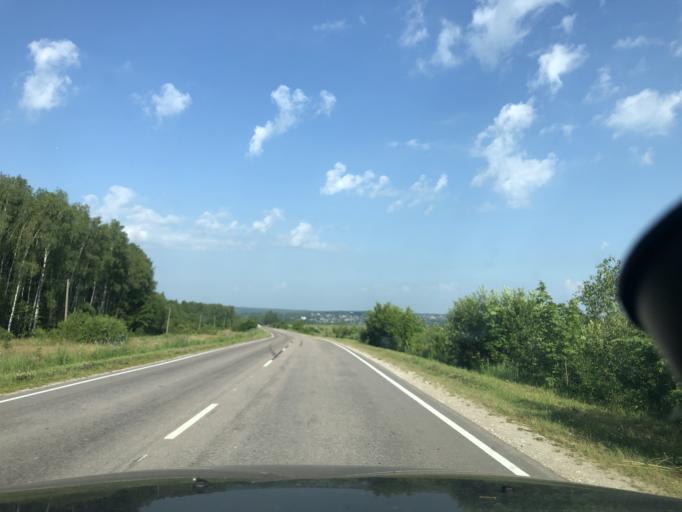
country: RU
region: Tula
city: Dubna
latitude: 54.1411
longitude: 37.0090
